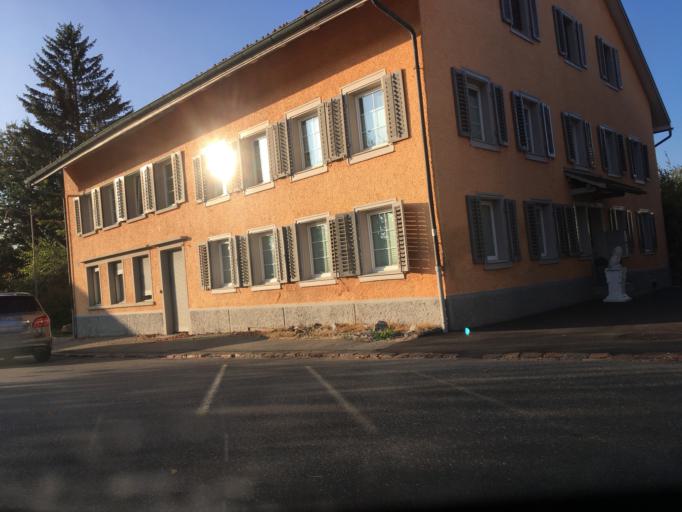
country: CH
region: Zurich
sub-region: Bezirk Pfaeffikon
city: Hittnau / Hittnau (Dorf)
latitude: 47.3609
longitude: 8.8232
